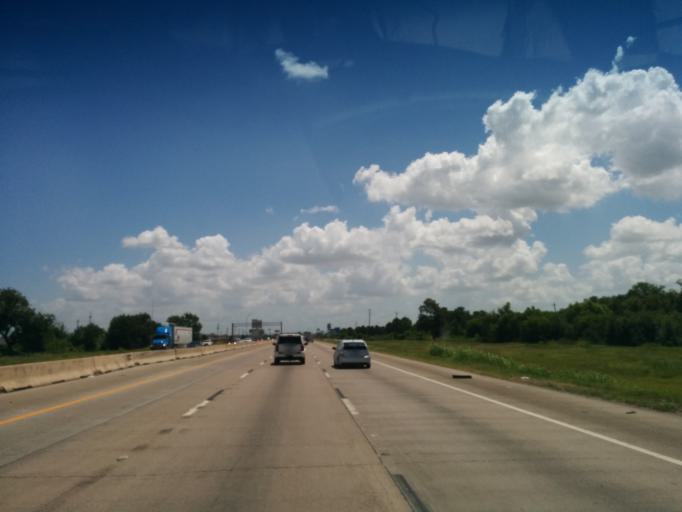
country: US
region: Texas
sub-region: Harris County
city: Highlands
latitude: 29.7932
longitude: -95.0435
